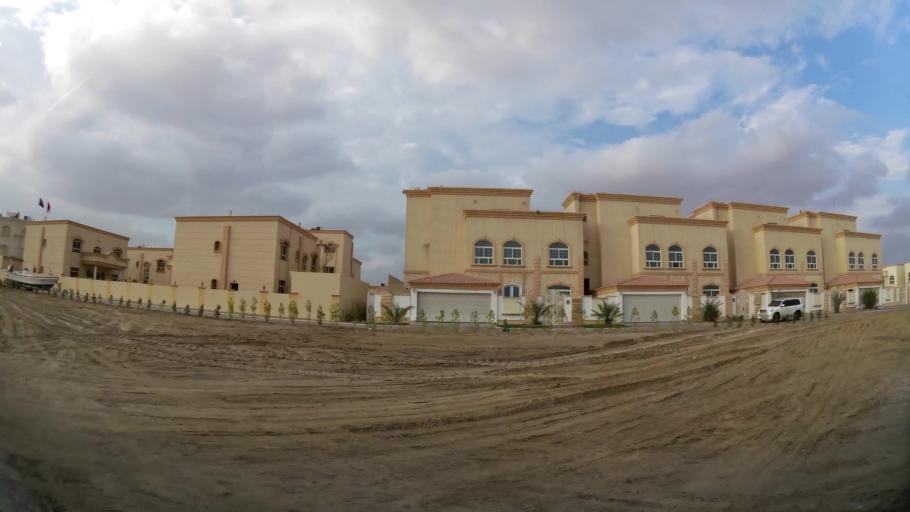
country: AE
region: Abu Dhabi
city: Abu Dhabi
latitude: 24.3528
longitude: 54.5537
